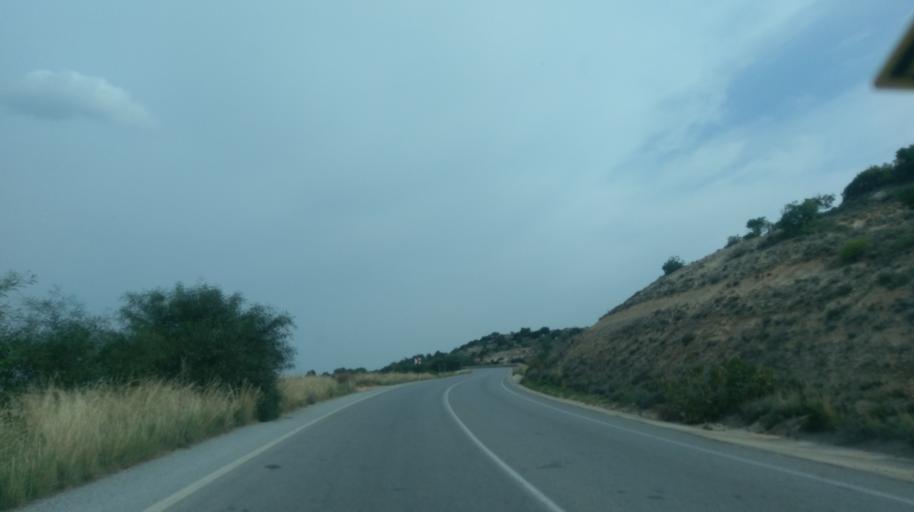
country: CY
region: Ammochostos
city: Trikomo
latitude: 35.2772
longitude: 33.8343
